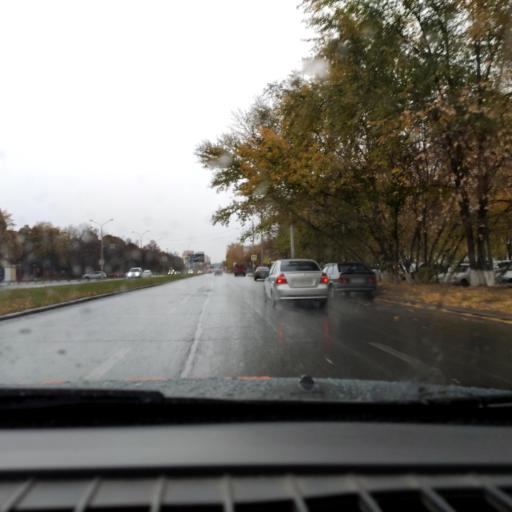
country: RU
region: Samara
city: Tol'yatti
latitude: 53.5160
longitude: 49.2656
